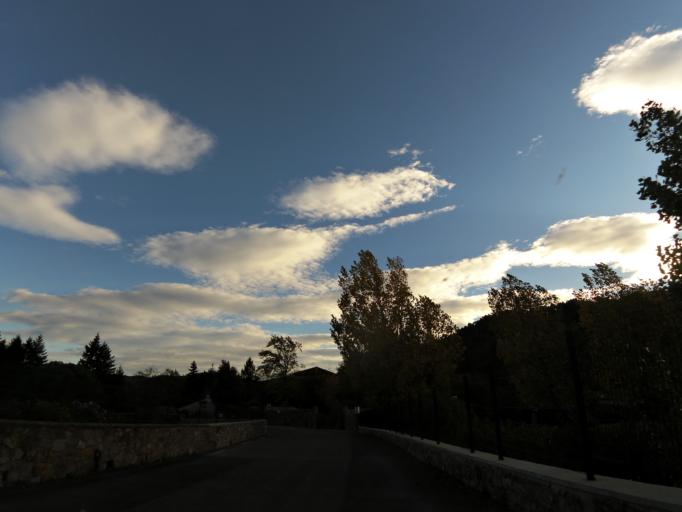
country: FR
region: Languedoc-Roussillon
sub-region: Departement du Gard
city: Lasalle
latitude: 44.0455
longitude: 3.8570
